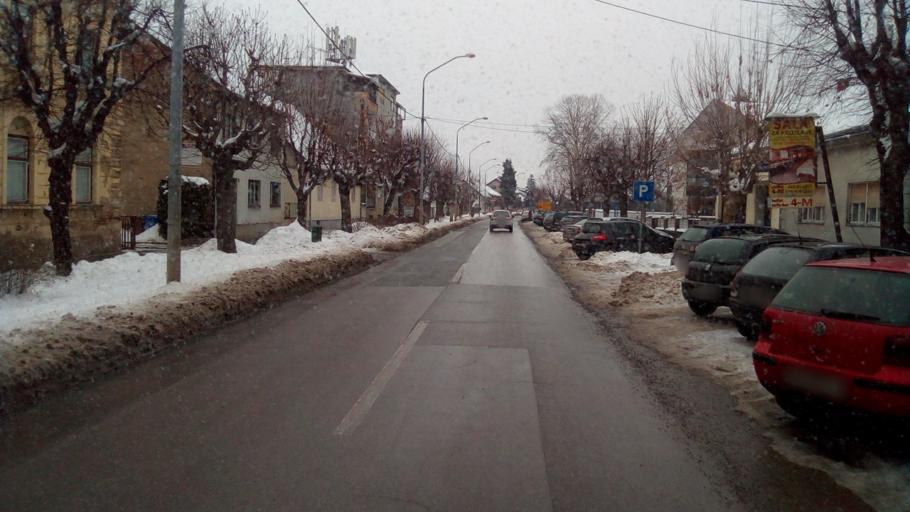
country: HR
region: Sisacko-Moslavacka
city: Petrinja
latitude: 45.4419
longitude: 16.2825
